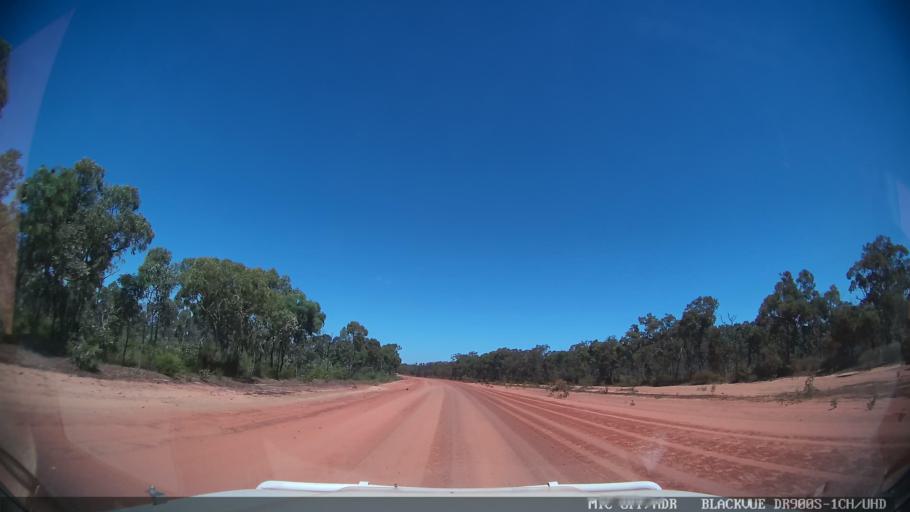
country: AU
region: Queensland
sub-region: Torres
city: Thursday Island
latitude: -11.3630
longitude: 142.3457
